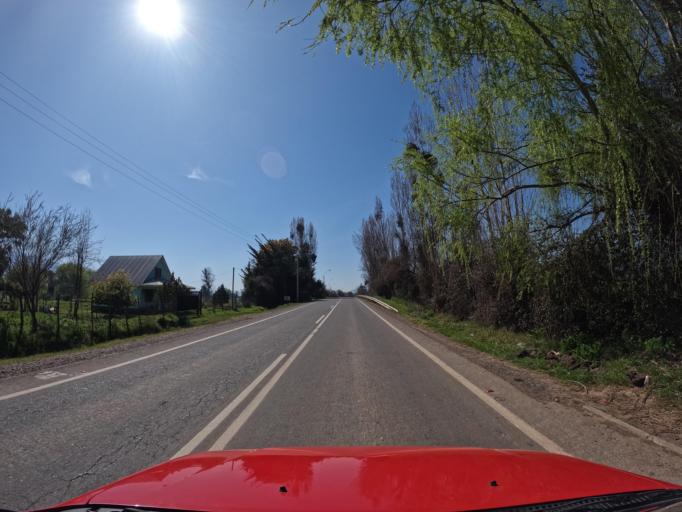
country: CL
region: Maule
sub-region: Provincia de Curico
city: Molina
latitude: -35.0534
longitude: -71.4801
